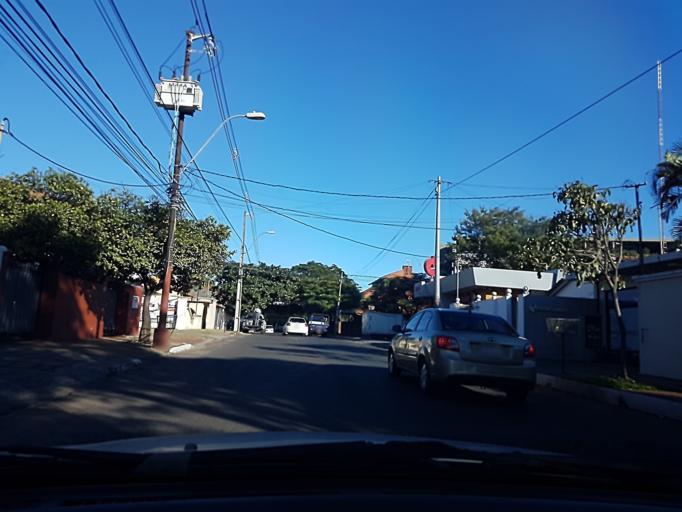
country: PY
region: Asuncion
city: Asuncion
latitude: -25.2797
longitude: -57.5727
